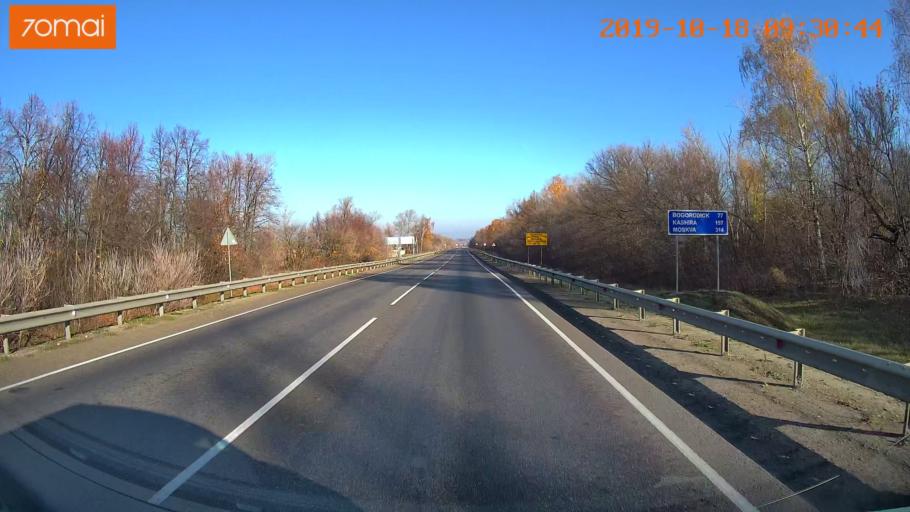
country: RU
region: Tula
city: Yefremov
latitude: 53.1416
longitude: 38.1594
